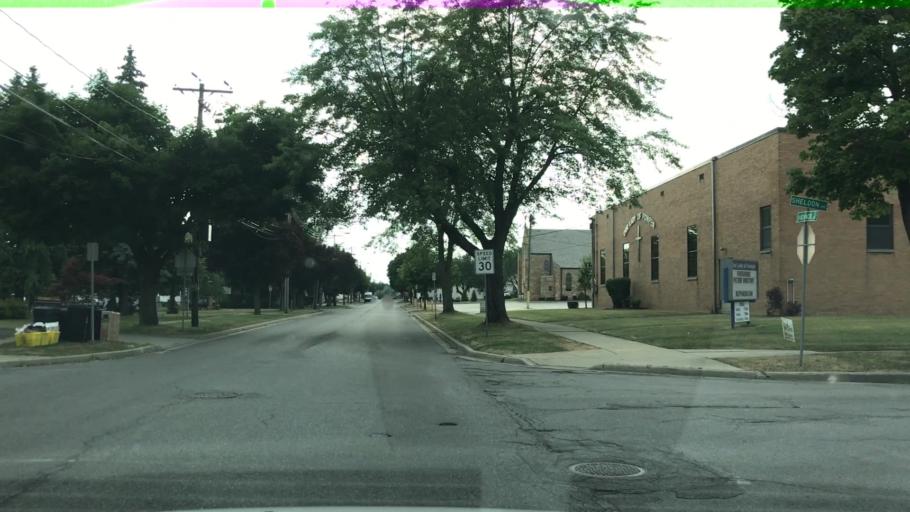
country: US
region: New York
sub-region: Erie County
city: Lancaster
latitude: 42.9078
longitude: -78.6782
